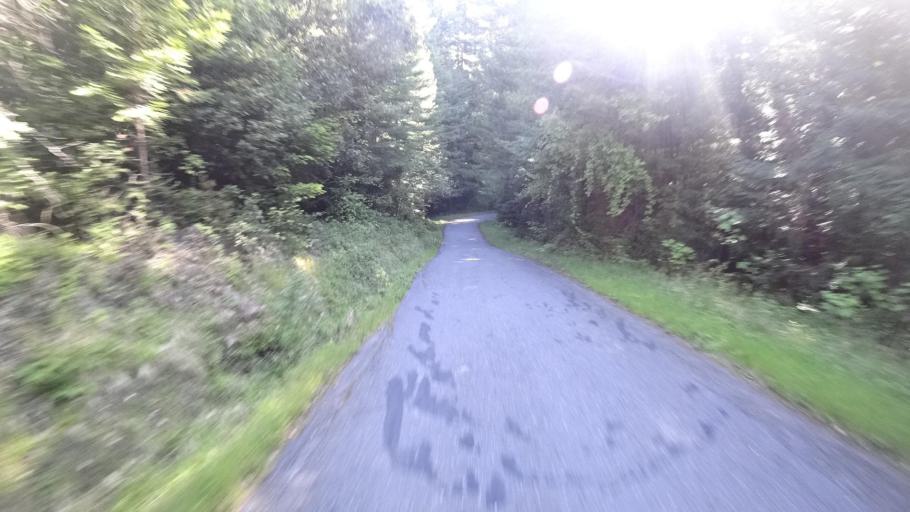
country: US
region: California
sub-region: Humboldt County
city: Rio Dell
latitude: 40.4603
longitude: -124.0048
